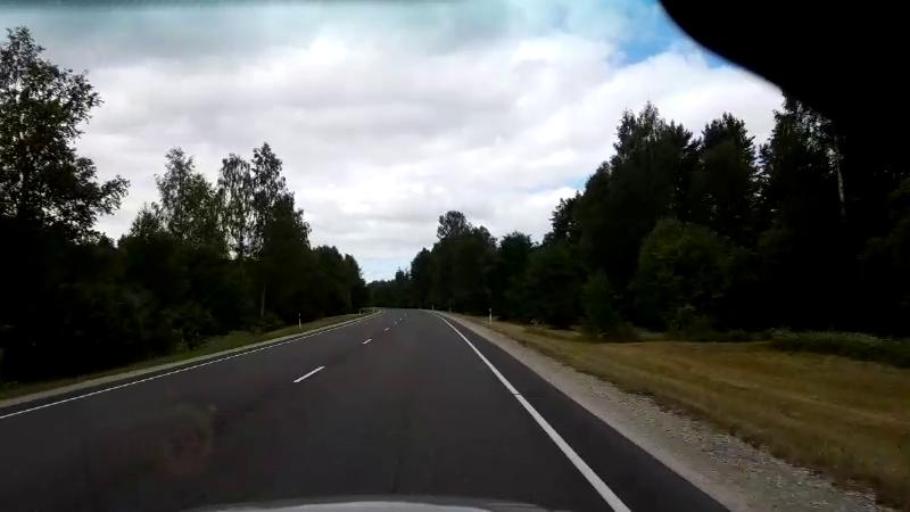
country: EE
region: Paernumaa
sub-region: Paernu linn
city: Parnu
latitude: 58.2517
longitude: 24.5248
